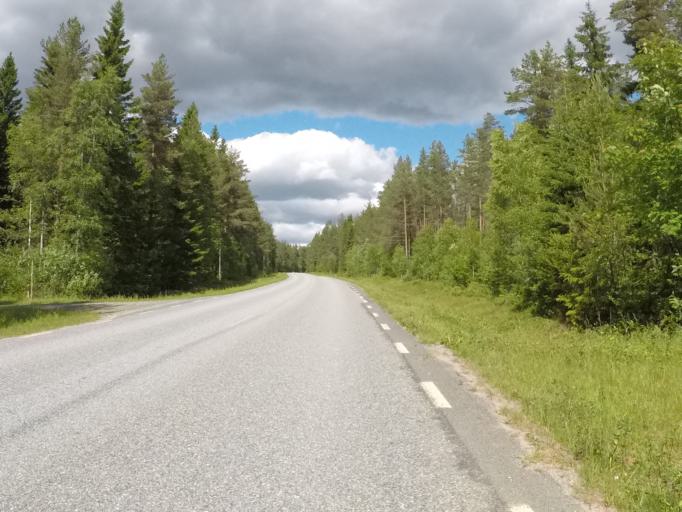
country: SE
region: Vaesterbotten
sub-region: Robertsfors Kommun
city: Robertsfors
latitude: 63.9706
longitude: 20.8118
